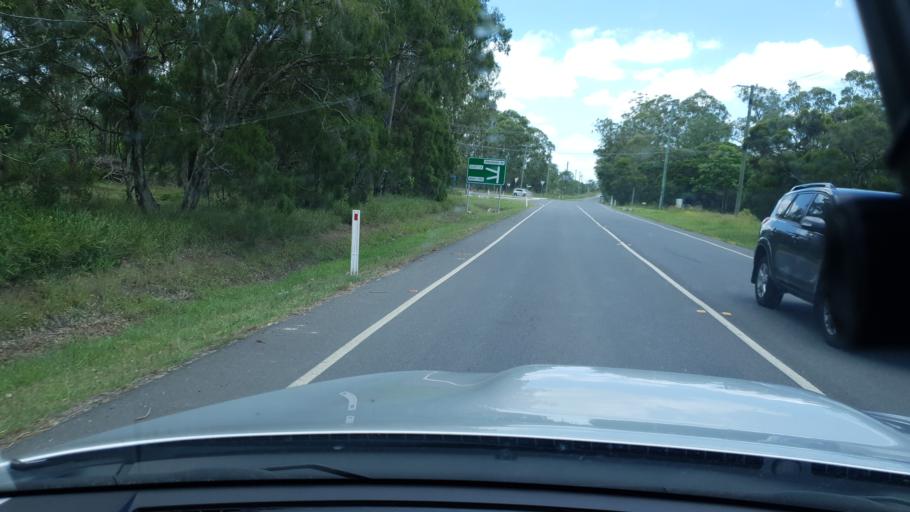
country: AU
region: Queensland
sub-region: Logan
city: North Maclean
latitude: -27.7753
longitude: 153.0096
